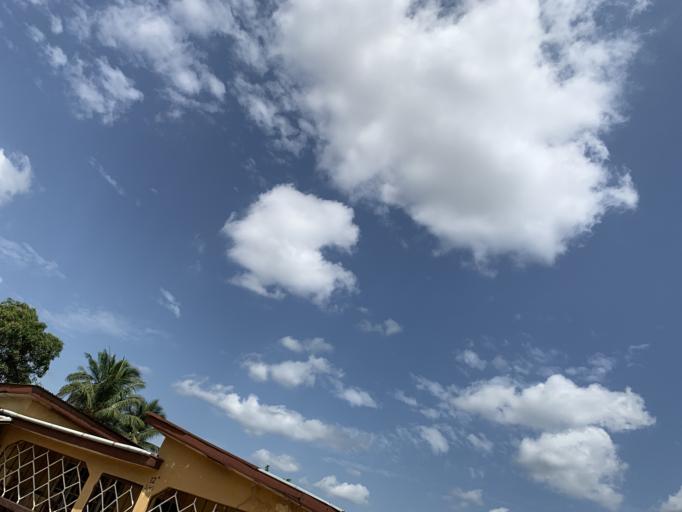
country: SL
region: Western Area
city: Waterloo
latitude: 8.3269
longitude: -13.0519
